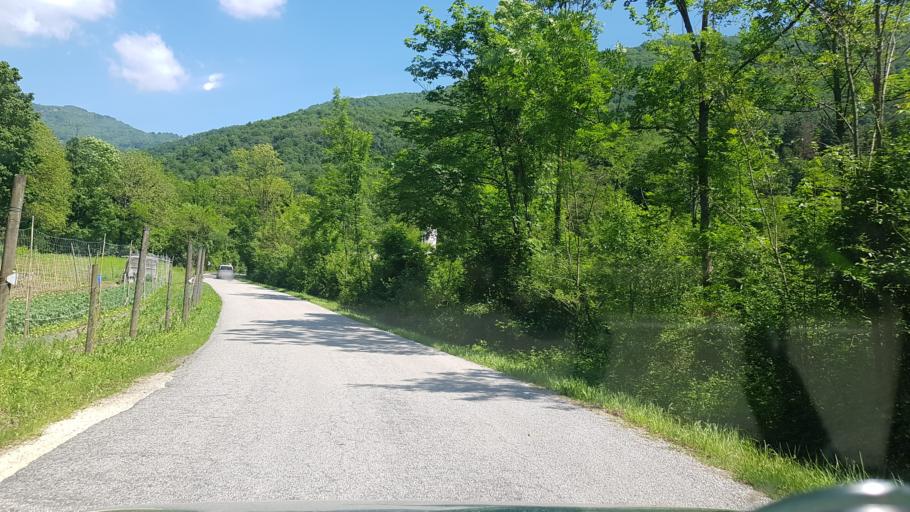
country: IT
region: Friuli Venezia Giulia
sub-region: Provincia di Udine
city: Torreano
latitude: 46.1472
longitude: 13.4381
